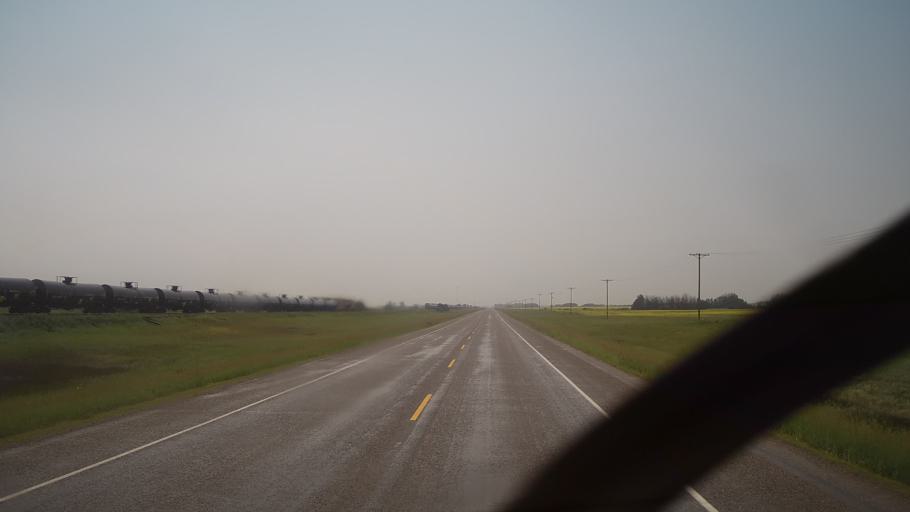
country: CA
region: Saskatchewan
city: Biggar
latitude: 52.1632
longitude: -108.2905
